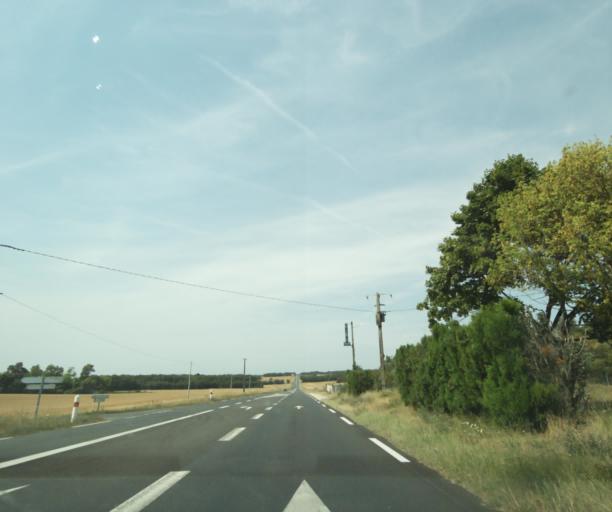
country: FR
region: Centre
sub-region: Departement d'Indre-et-Loire
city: Sainte-Maure-de-Touraine
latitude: 47.0744
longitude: 0.6135
